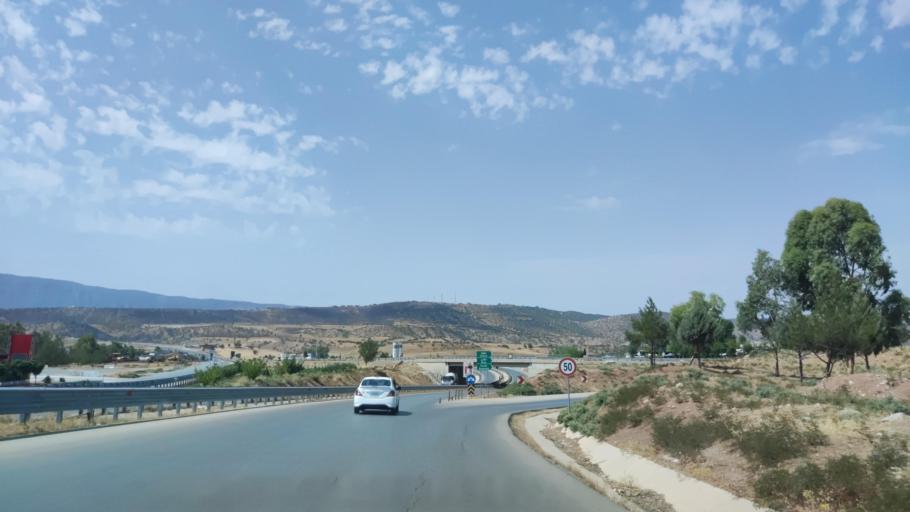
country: IQ
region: Arbil
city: Shaqlawah
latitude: 36.4581
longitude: 44.3861
